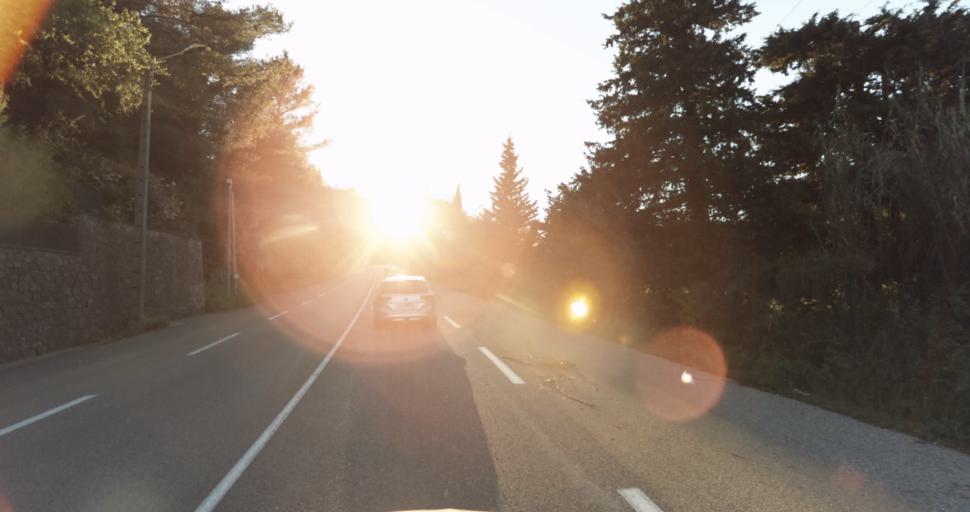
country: FR
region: Provence-Alpes-Cote d'Azur
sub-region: Departement du Var
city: La Valette-du-Var
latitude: 43.1524
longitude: 5.9670
